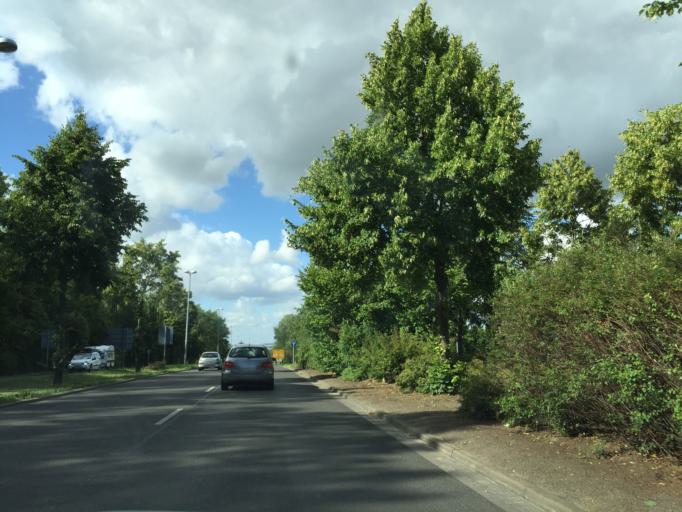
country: DE
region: Mecklenburg-Vorpommern
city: Neubrandenburg
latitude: 53.5265
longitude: 13.2620
